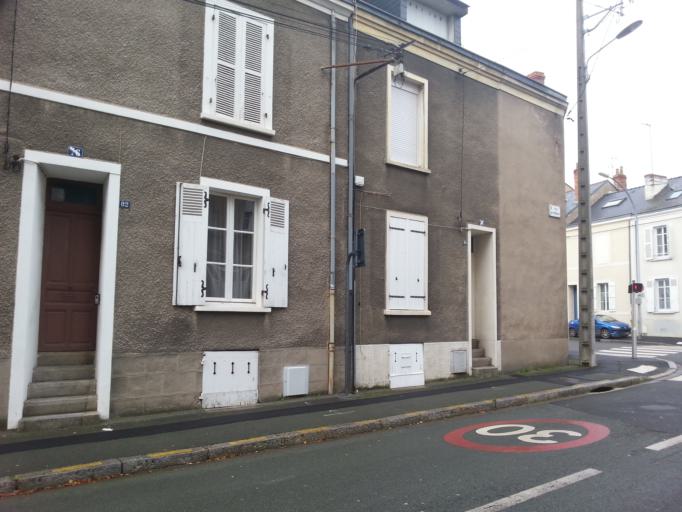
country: FR
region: Pays de la Loire
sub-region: Departement de Maine-et-Loire
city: Angers
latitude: 47.4585
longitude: -0.5587
